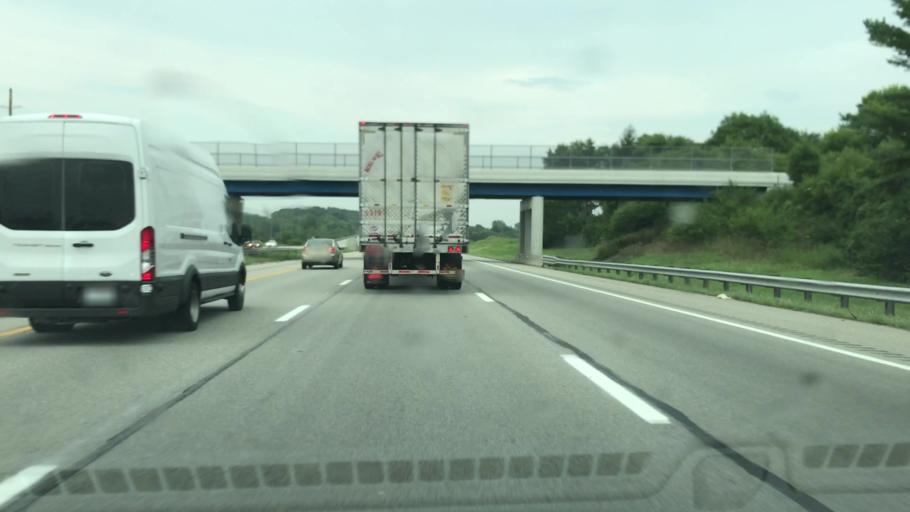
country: US
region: Ohio
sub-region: Clark County
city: Springfield
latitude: 39.8898
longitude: -83.7740
